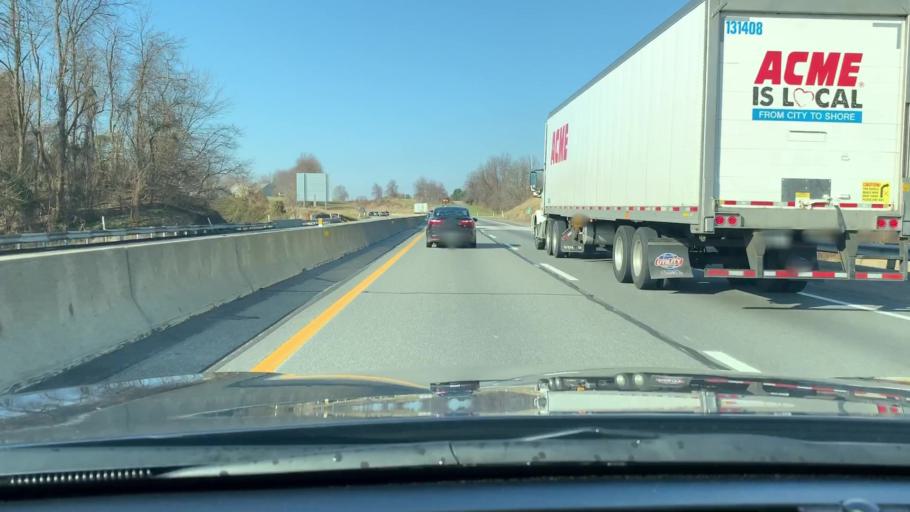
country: US
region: Pennsylvania
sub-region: Chester County
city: Downingtown
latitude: 40.0814
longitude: -75.7069
